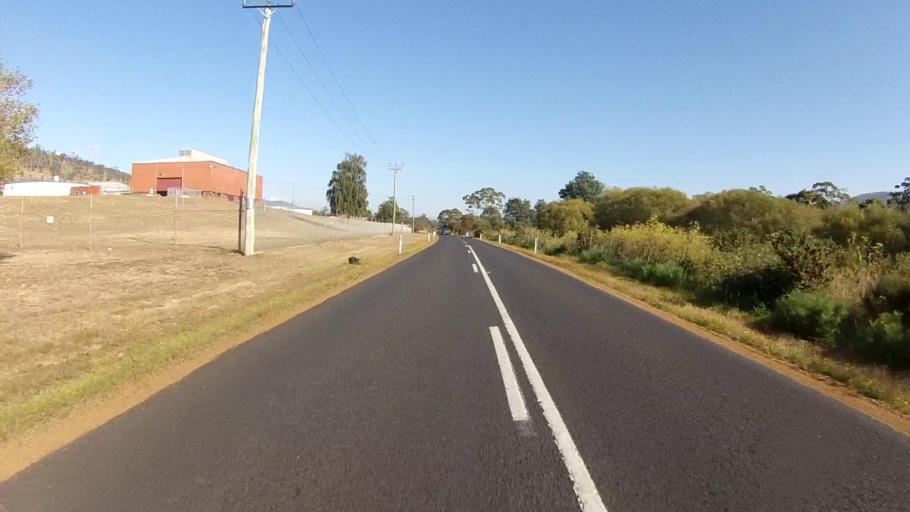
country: AU
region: Tasmania
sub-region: Derwent Valley
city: New Norfolk
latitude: -42.7679
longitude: 147.0232
